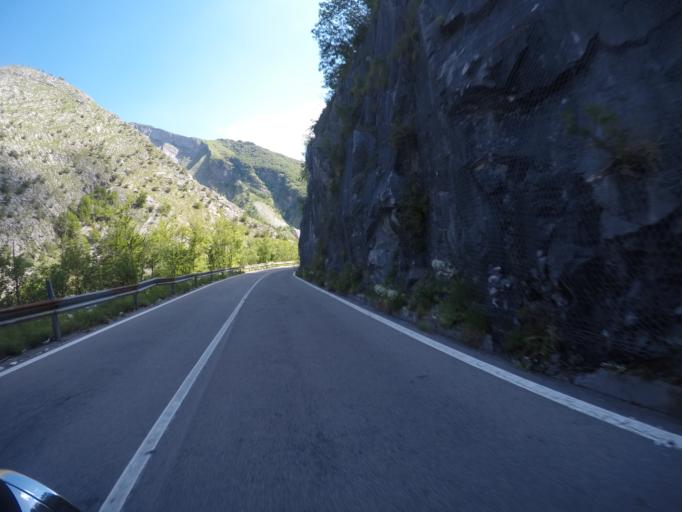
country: IT
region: Tuscany
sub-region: Provincia di Lucca
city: Fontana delle Monache
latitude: 44.0604
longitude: 10.2808
